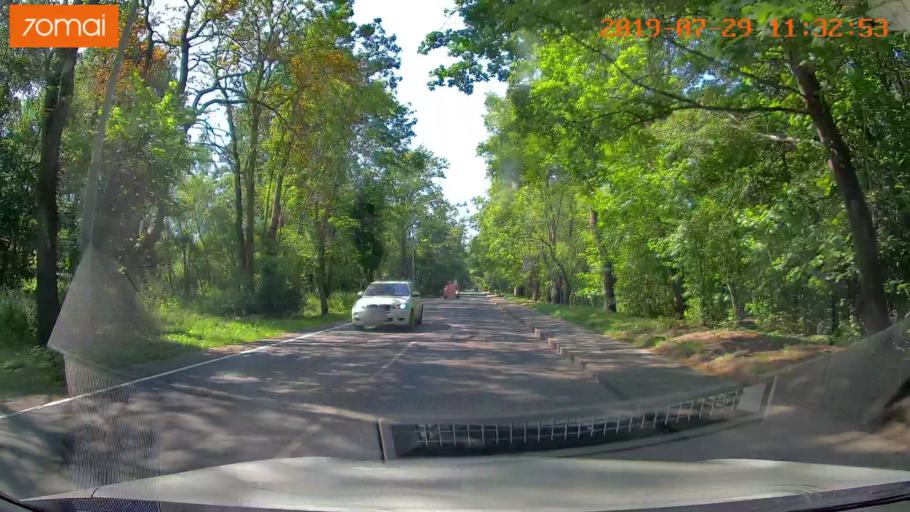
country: RU
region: Kaliningrad
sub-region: Gorod Kaliningrad
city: Kaliningrad
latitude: 54.6687
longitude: 20.5447
